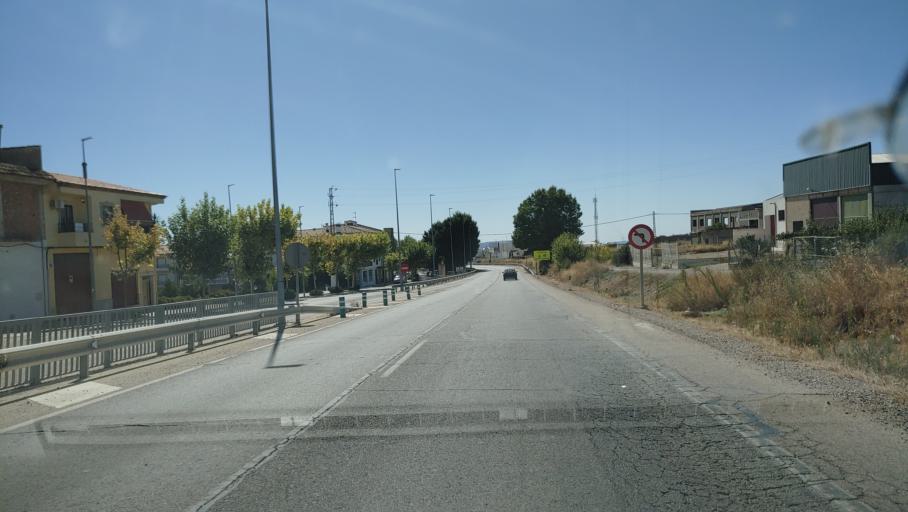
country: ES
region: Andalusia
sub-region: Provincia de Jaen
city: Villacarrillo
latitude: 38.1224
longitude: -3.0709
